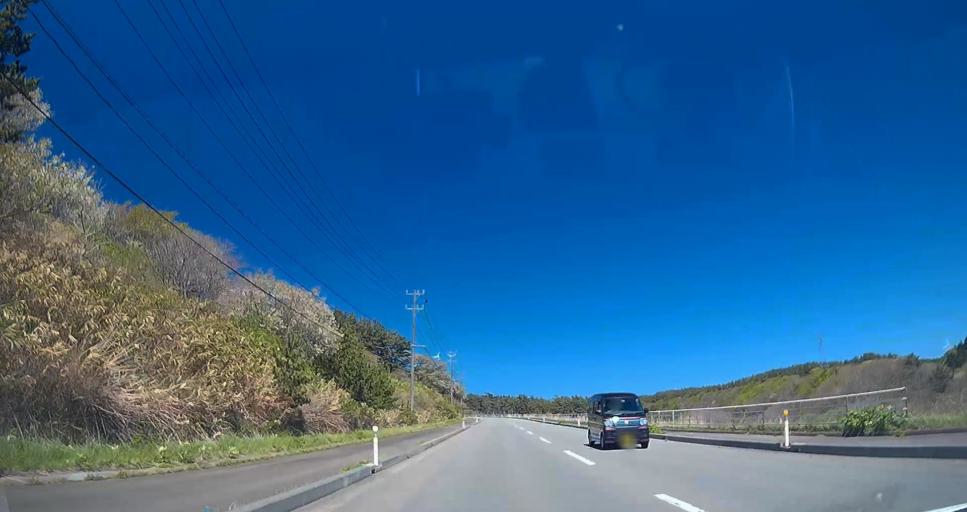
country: JP
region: Hokkaido
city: Hakodate
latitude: 41.5045
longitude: 140.9131
